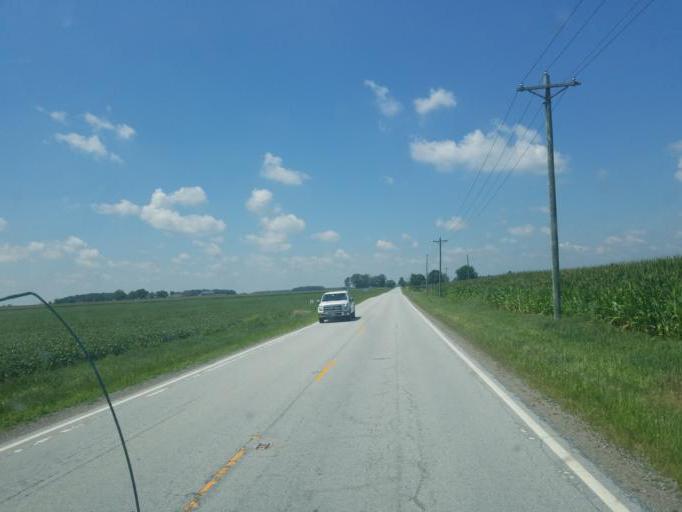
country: US
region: Ohio
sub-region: Allen County
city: Spencerville
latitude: 40.7140
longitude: -84.4178
